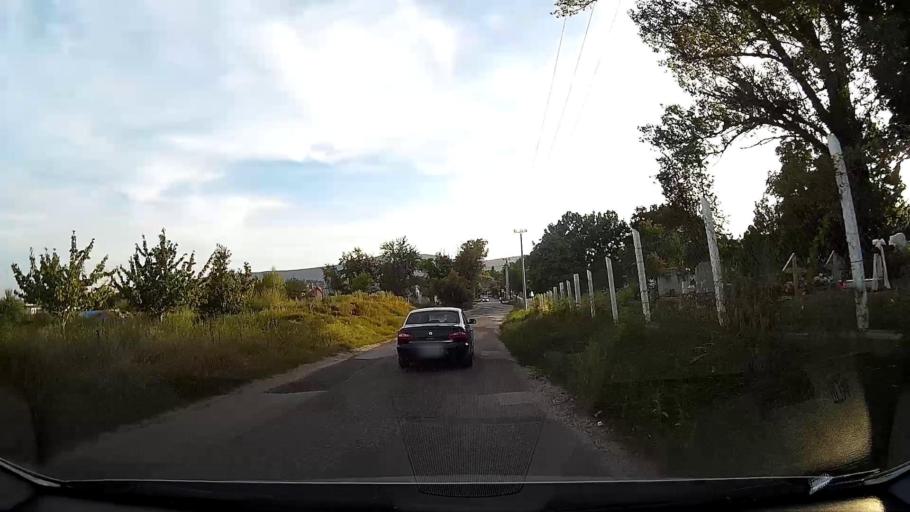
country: HU
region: Pest
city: Nagykovacsi
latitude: 47.6542
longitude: 19.0242
